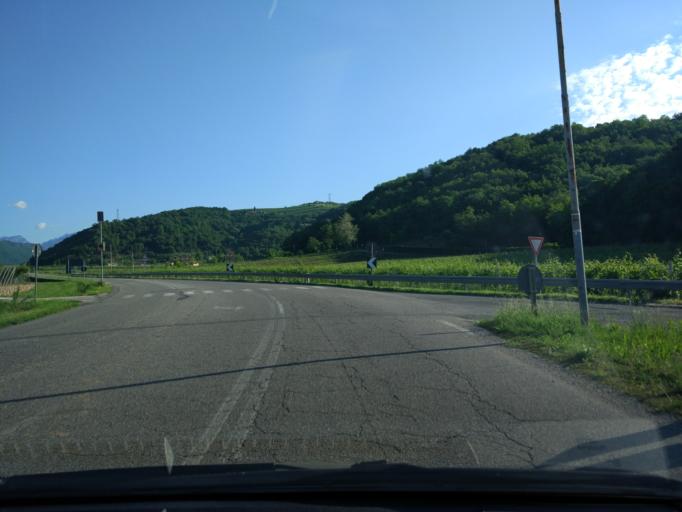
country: IT
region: Veneto
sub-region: Provincia di Verona
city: Tregnago
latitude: 45.5224
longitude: 11.1629
